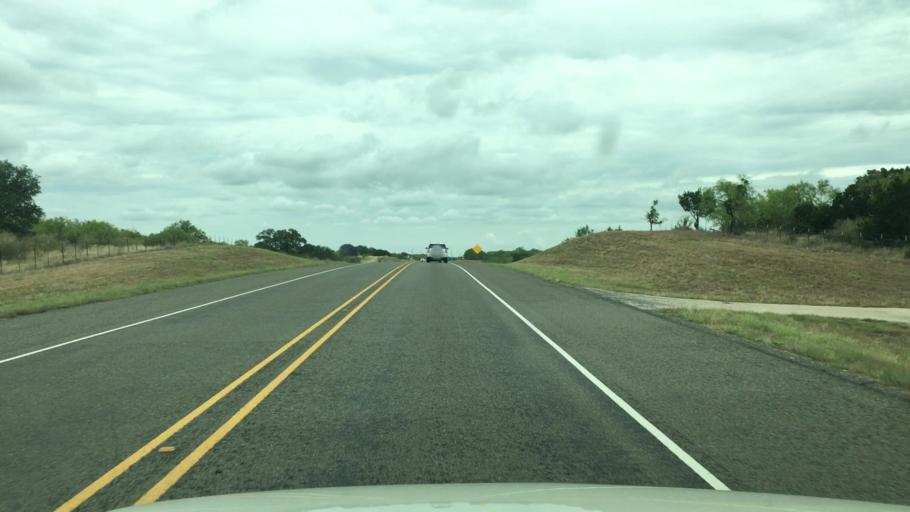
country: US
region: Texas
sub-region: Burnet County
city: Granite Shoals
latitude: 30.5648
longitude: -98.4805
